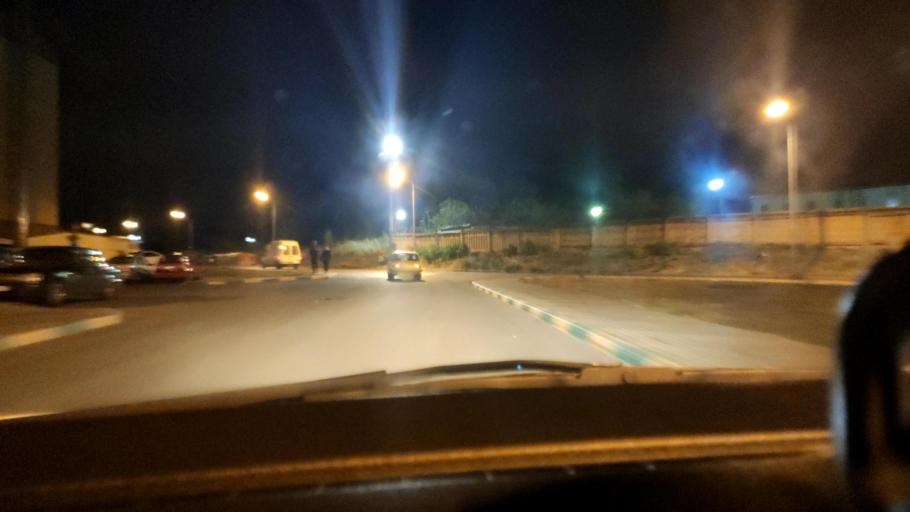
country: RU
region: Voronezj
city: Shilovo
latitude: 51.5713
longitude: 39.1268
